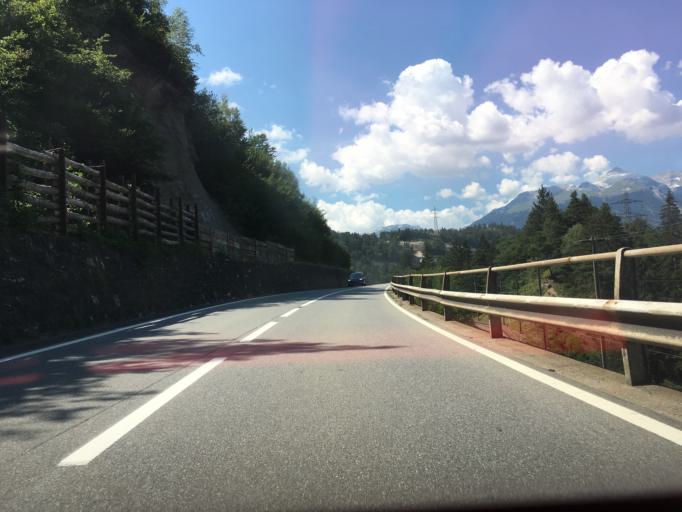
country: CH
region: Grisons
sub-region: Imboden District
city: Rhazuns
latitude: 46.7767
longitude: 9.4122
